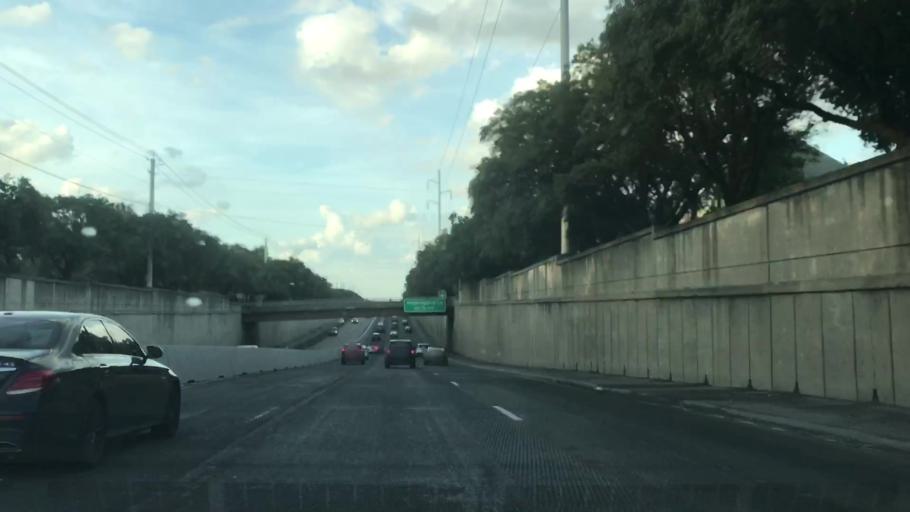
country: US
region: Texas
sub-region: Dallas County
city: Highland Park
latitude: 32.8257
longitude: -96.8163
